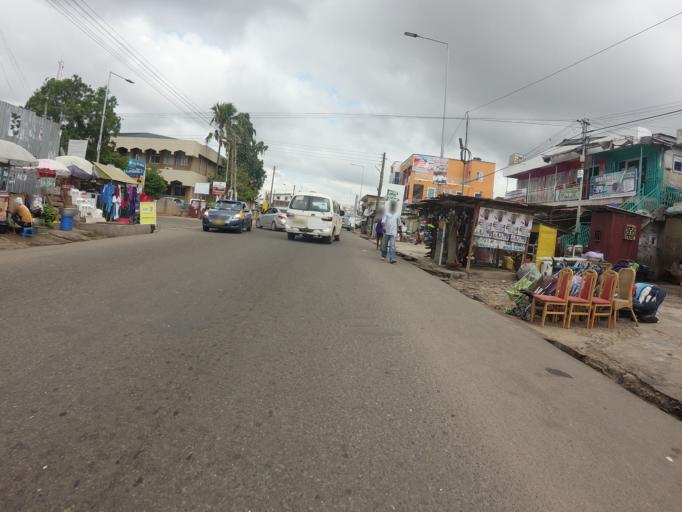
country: GH
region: Greater Accra
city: Accra
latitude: 5.5846
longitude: -0.2081
